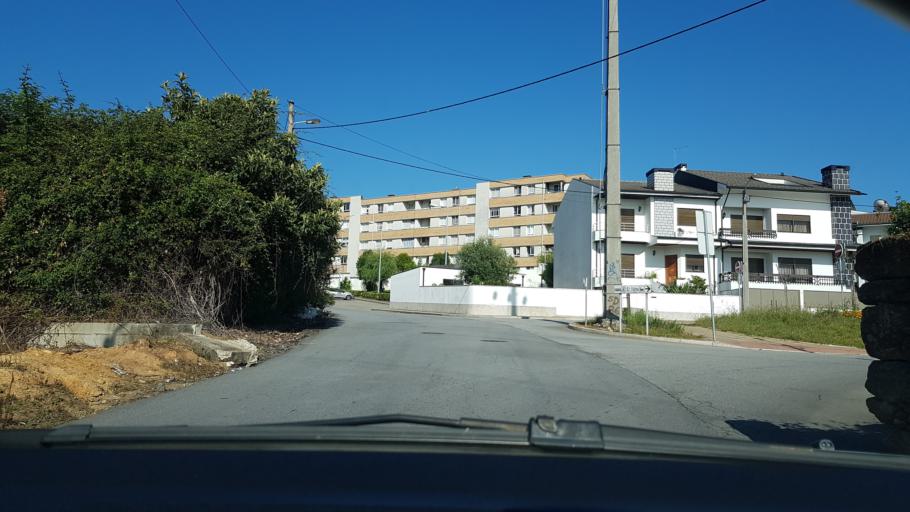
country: PT
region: Porto
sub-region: Gondomar
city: Baguim do Monte
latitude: 41.1885
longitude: -8.5288
